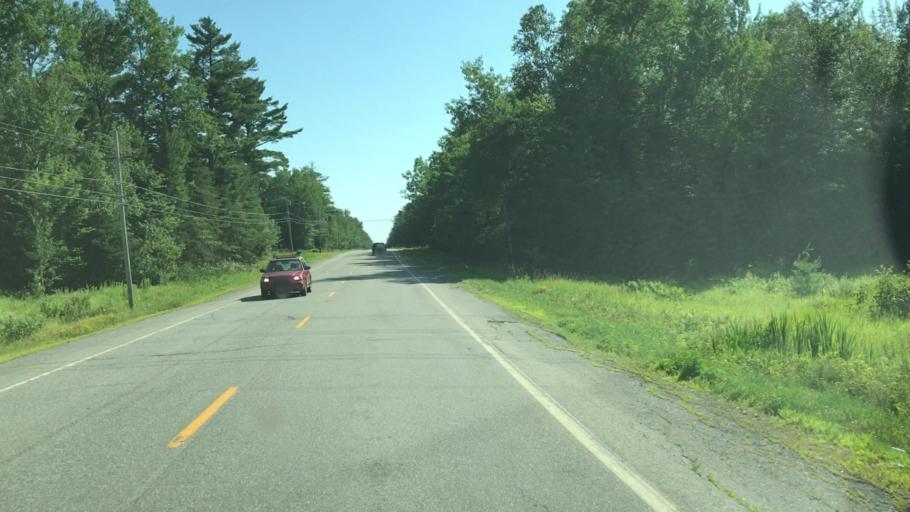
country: US
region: Maine
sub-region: Penobscot County
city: Enfield
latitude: 45.3193
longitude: -68.6001
